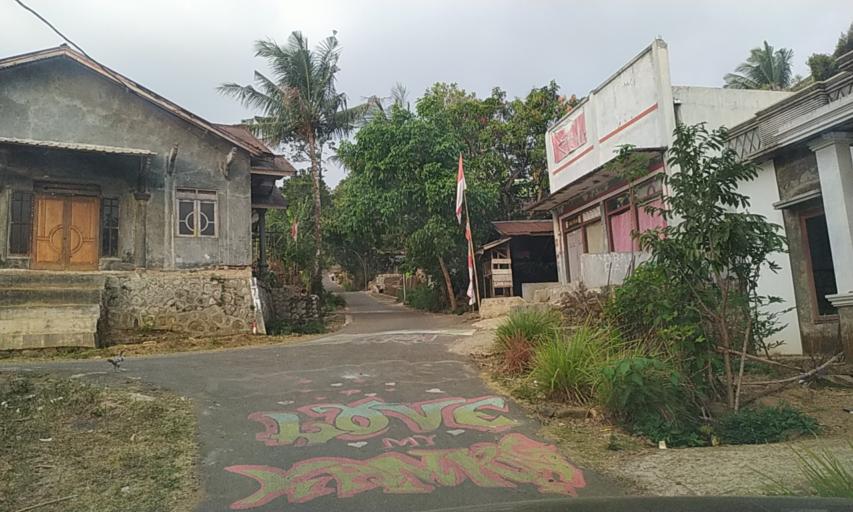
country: ID
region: Central Java
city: Randudongkal
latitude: -7.1483
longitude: 109.3749
